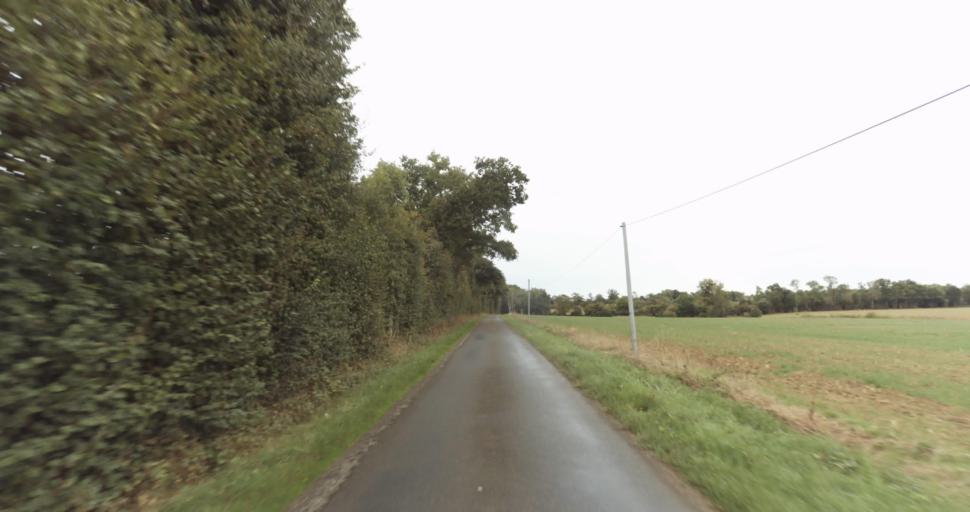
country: FR
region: Lower Normandy
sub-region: Departement de l'Orne
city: Gace
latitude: 48.7250
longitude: 0.2908
